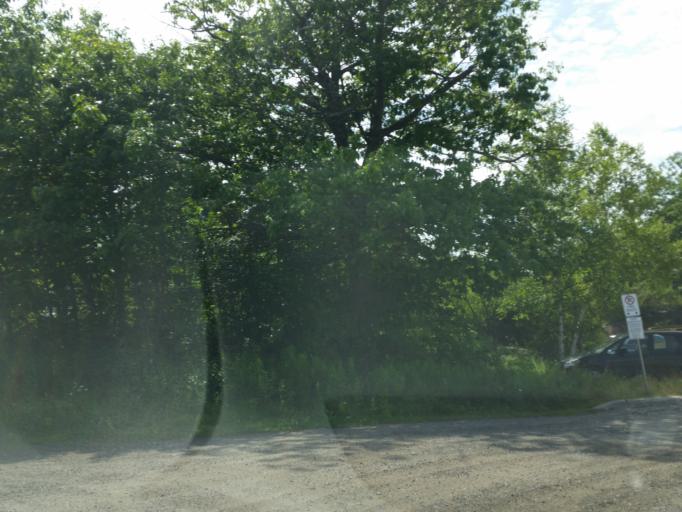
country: CA
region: Ontario
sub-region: Parry Sound District
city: Parry Sound
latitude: 45.3385
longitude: -80.0393
